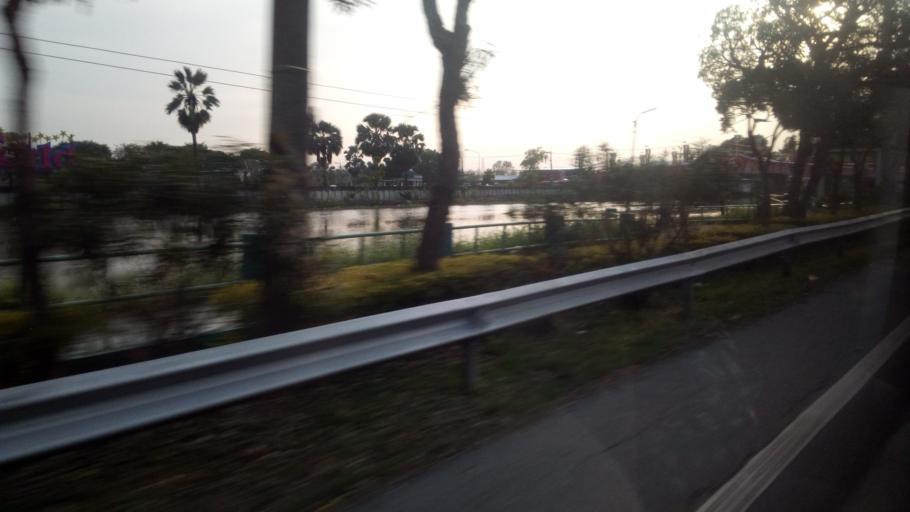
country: TH
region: Pathum Thani
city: Thanyaburi
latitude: 13.9975
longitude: 100.6758
